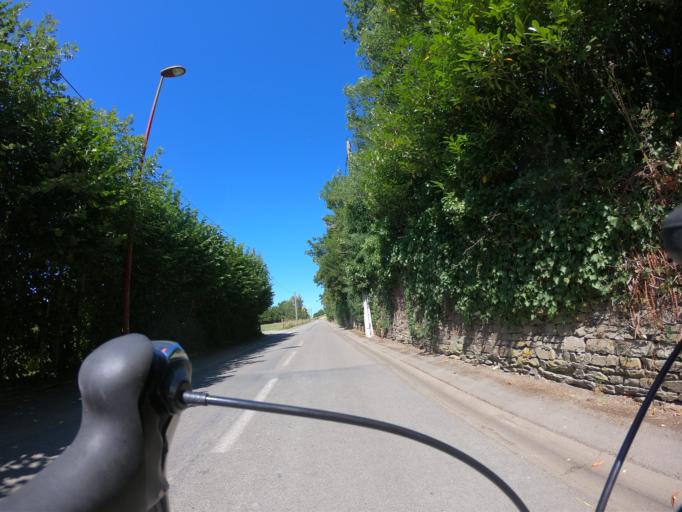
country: FR
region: Lower Normandy
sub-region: Departement de la Manche
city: Pontorson
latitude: 48.5875
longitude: -1.4791
